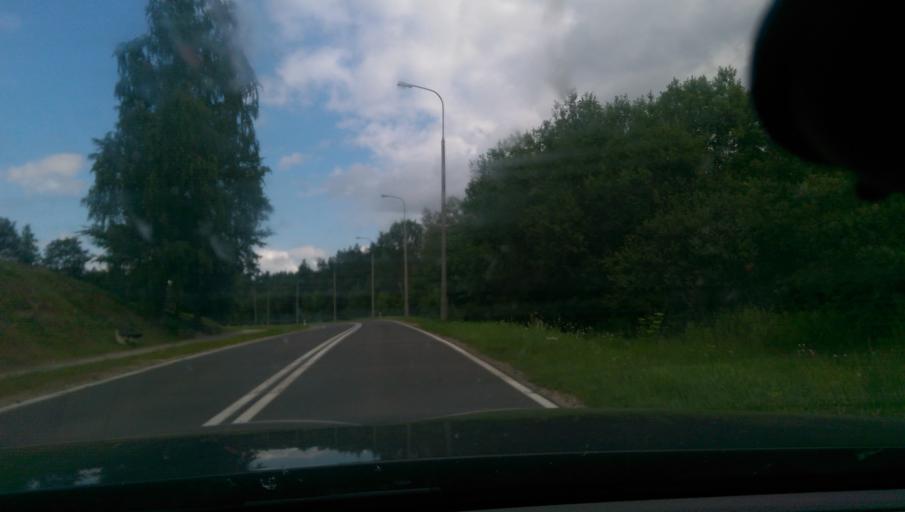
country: PL
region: Warmian-Masurian Voivodeship
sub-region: Powiat goldapski
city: Goldap
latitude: 54.3228
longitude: 22.2981
